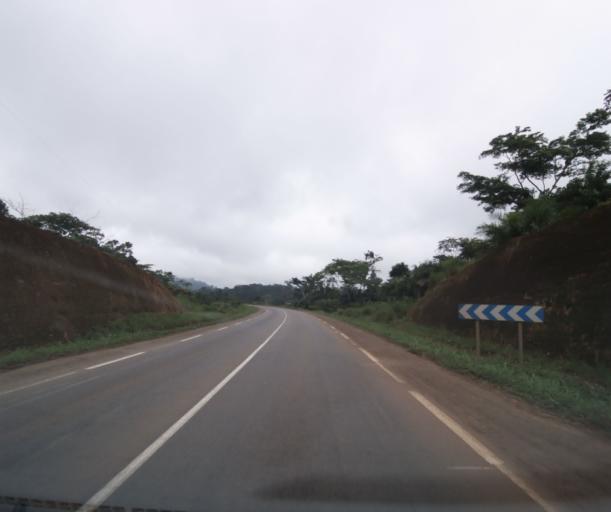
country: CM
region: Centre
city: Mbankomo
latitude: 3.7647
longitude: 11.1139
